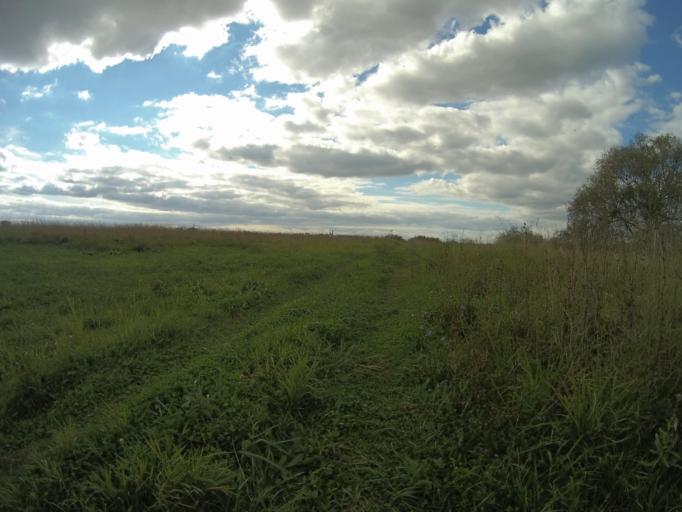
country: RU
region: Vladimir
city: Orgtrud
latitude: 56.3227
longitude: 40.6687
